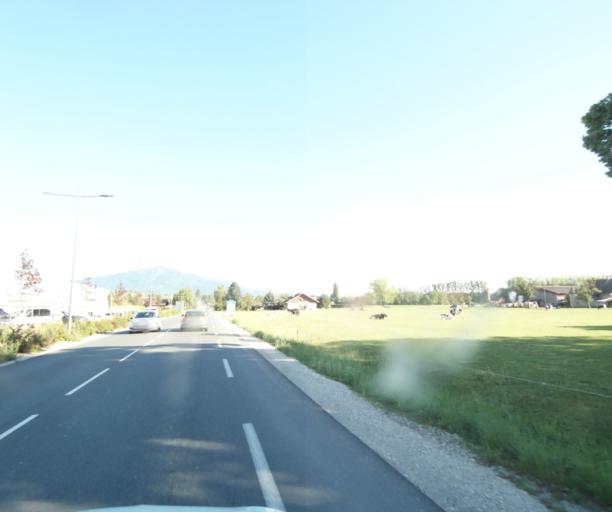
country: FR
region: Rhone-Alpes
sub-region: Departement de la Haute-Savoie
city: Douvaine
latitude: 46.3033
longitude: 6.3026
